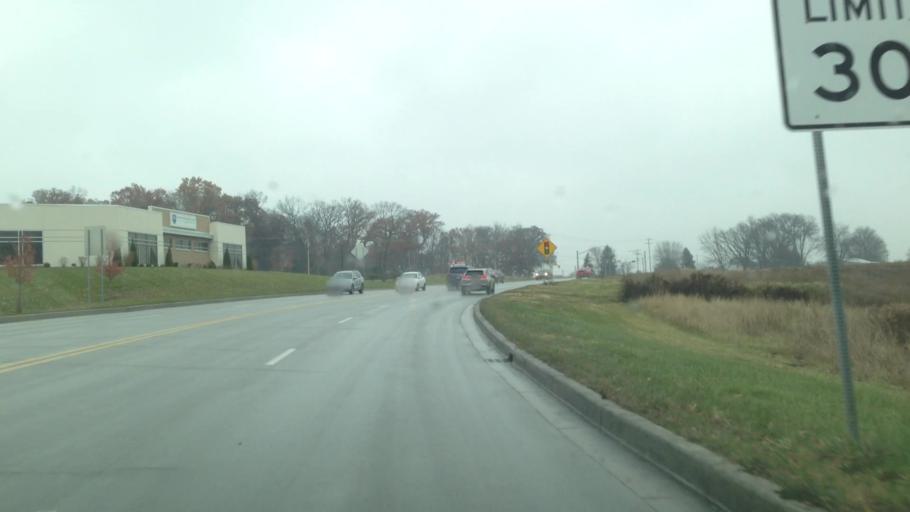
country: US
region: Indiana
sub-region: Saint Joseph County
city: Granger
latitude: 41.7226
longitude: -86.1626
